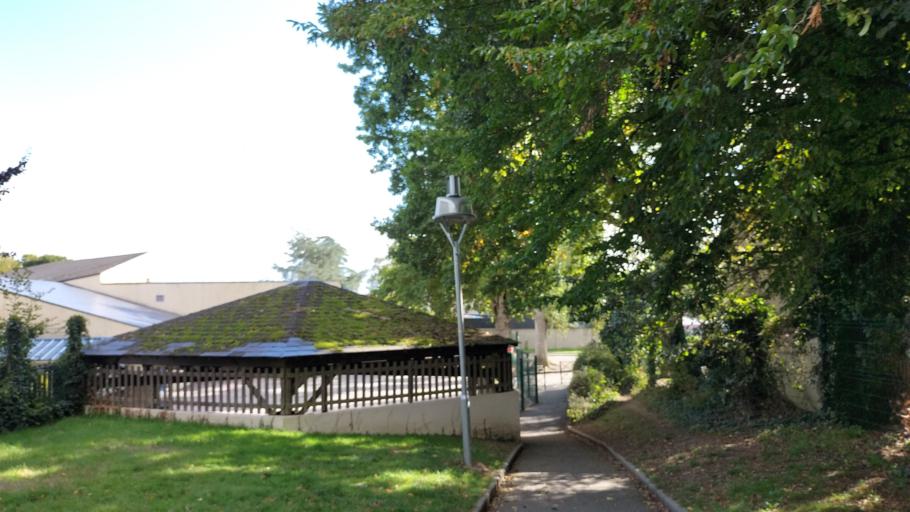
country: FR
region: Brittany
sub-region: Departement d'Ille-et-Vilaine
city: Liffre
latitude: 48.2118
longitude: -1.5067
